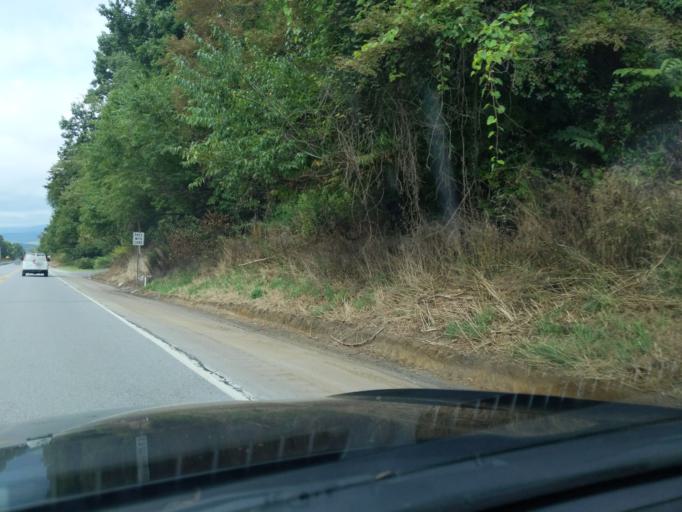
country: US
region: Pennsylvania
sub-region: Blair County
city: Hollidaysburg
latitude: 40.4077
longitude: -78.4015
